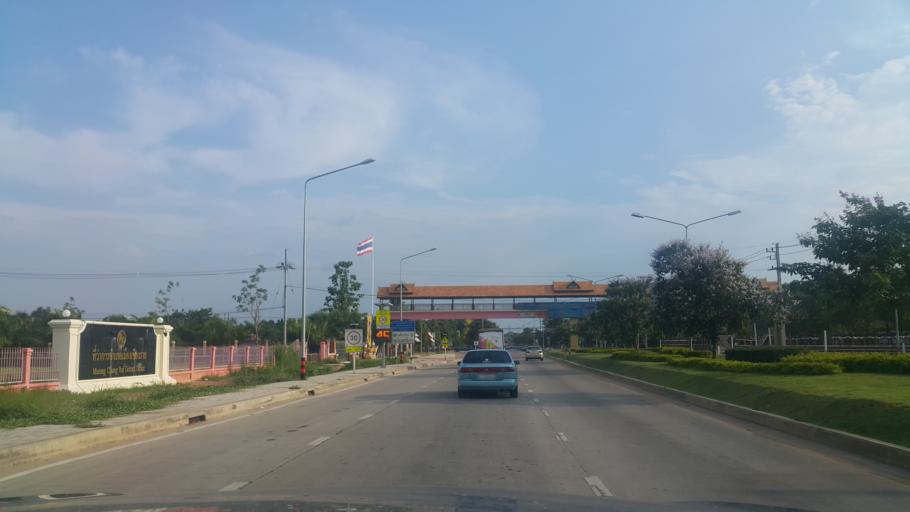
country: TH
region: Chiang Rai
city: Chiang Rai
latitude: 19.9294
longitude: 99.8638
